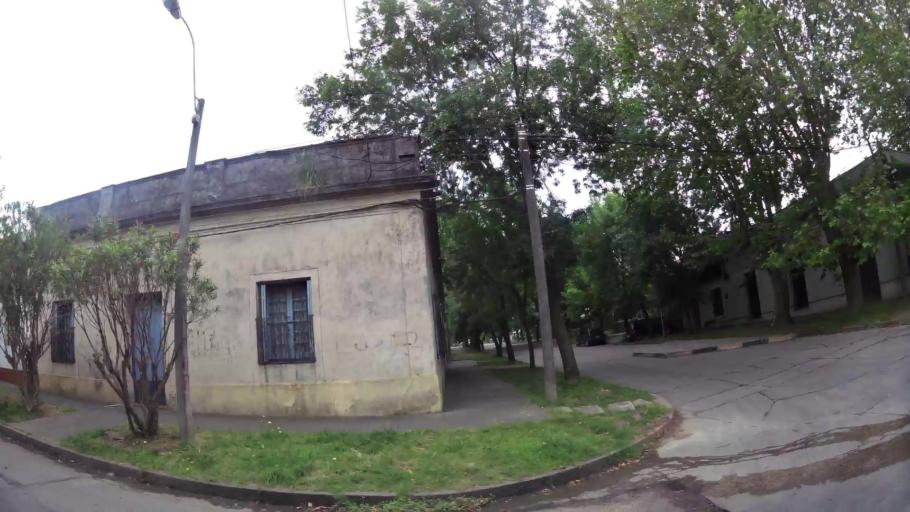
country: UY
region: Canelones
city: La Paz
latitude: -34.7600
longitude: -56.2249
